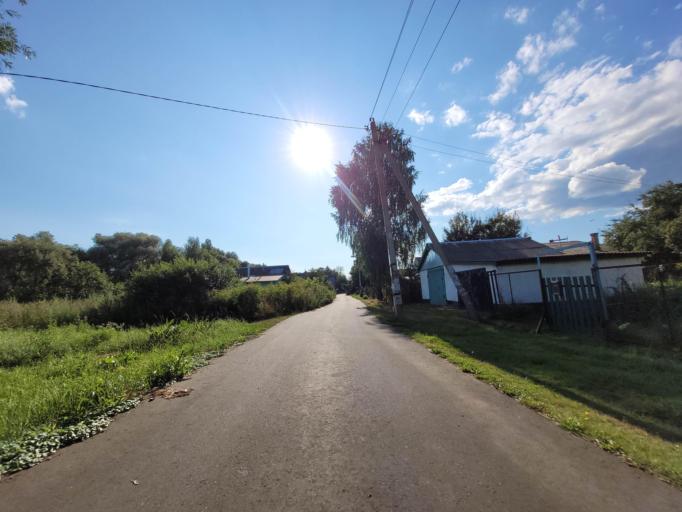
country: RU
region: Moskovskaya
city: Konobeyevo
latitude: 55.4148
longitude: 38.7045
